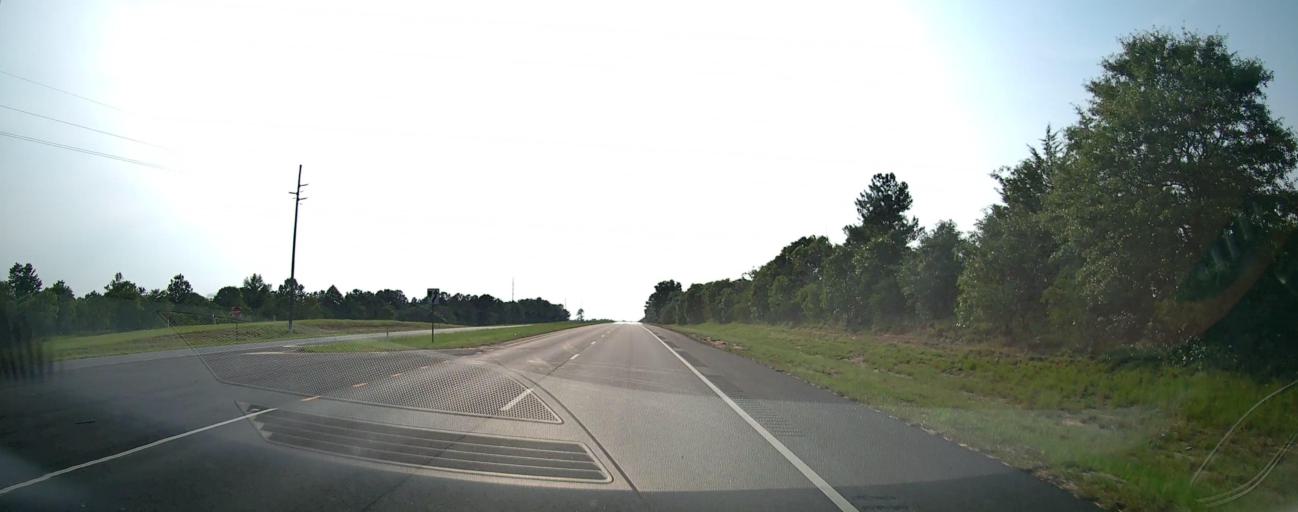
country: US
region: Georgia
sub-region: Taylor County
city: Butler
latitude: 32.5861
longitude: -84.3436
